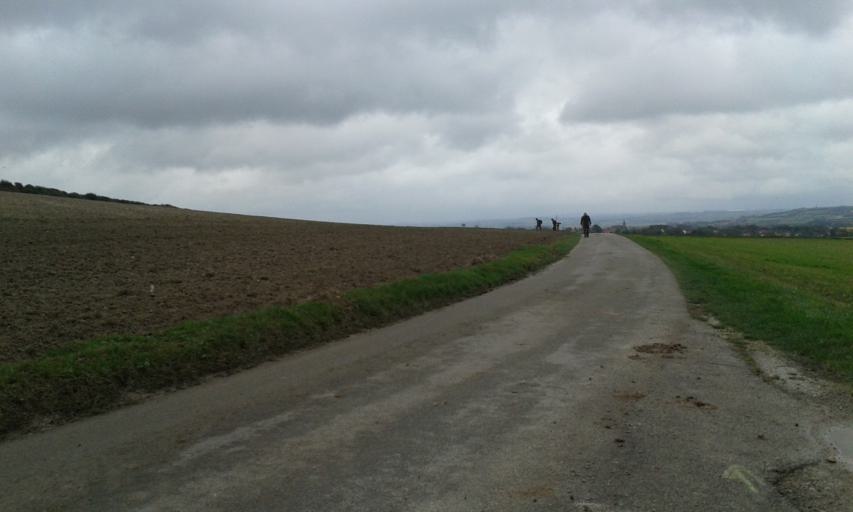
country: FR
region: Nord-Pas-de-Calais
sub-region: Departement du Pas-de-Calais
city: Wissant
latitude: 50.8740
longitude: 1.6981
